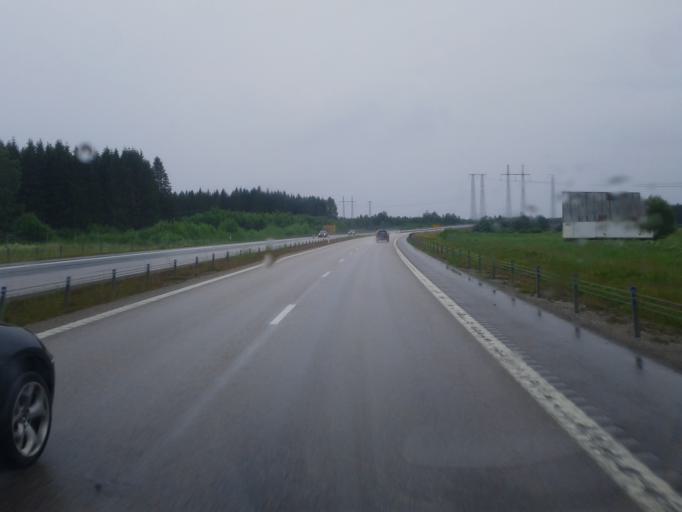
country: SE
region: Uppsala
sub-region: Tierps Kommun
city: Tierp
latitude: 60.3519
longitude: 17.4738
